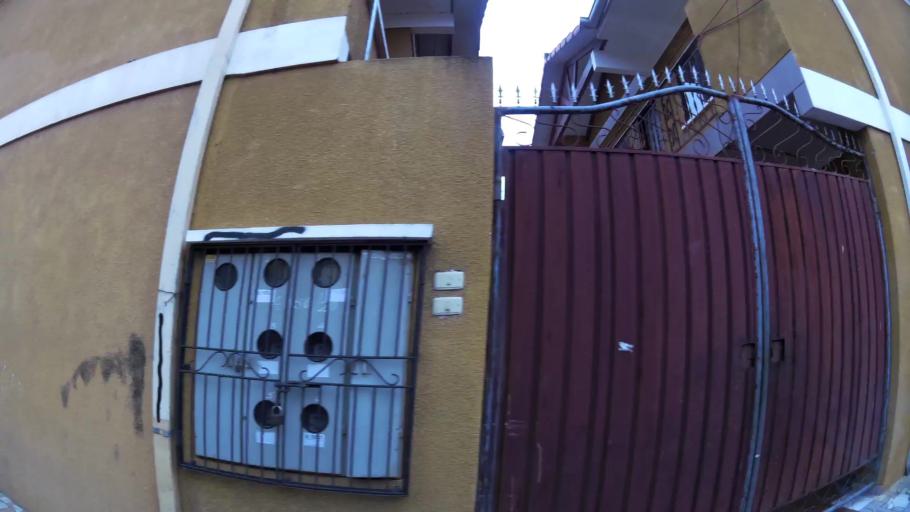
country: BO
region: Santa Cruz
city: Santa Cruz de la Sierra
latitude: -17.7790
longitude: -63.1629
